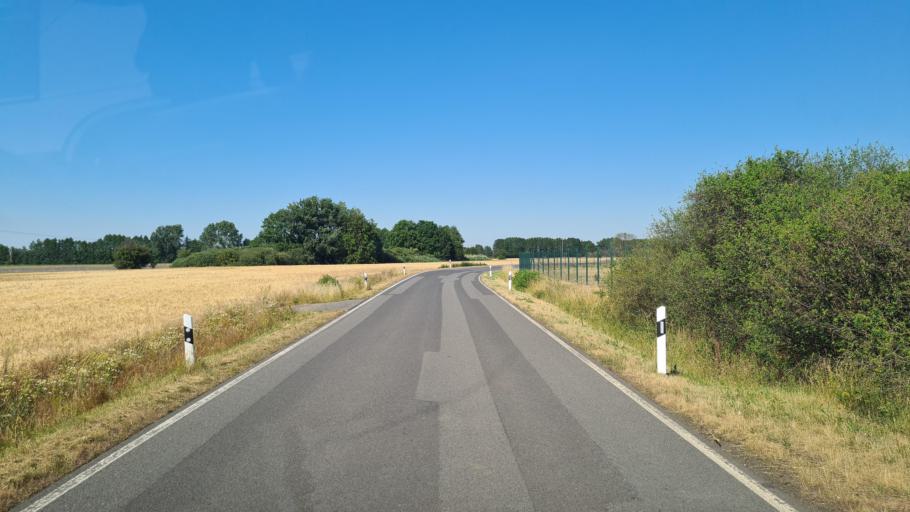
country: DE
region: Saxony-Anhalt
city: Prettin
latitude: 51.6965
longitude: 12.9779
